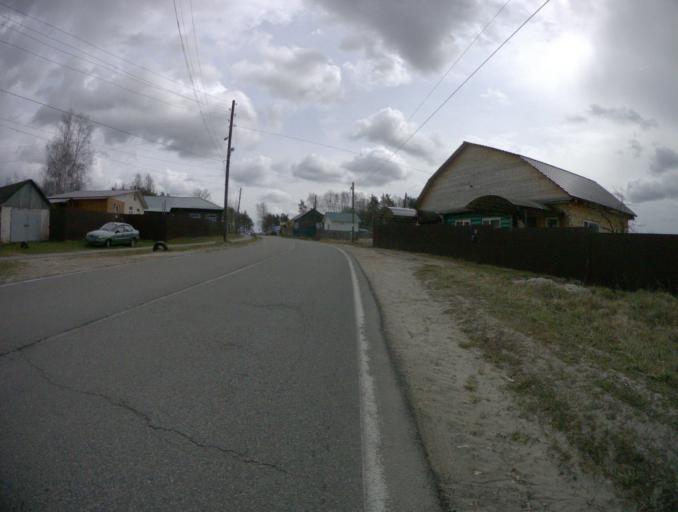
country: RU
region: Vladimir
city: Sudogda
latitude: 56.0722
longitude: 40.7883
